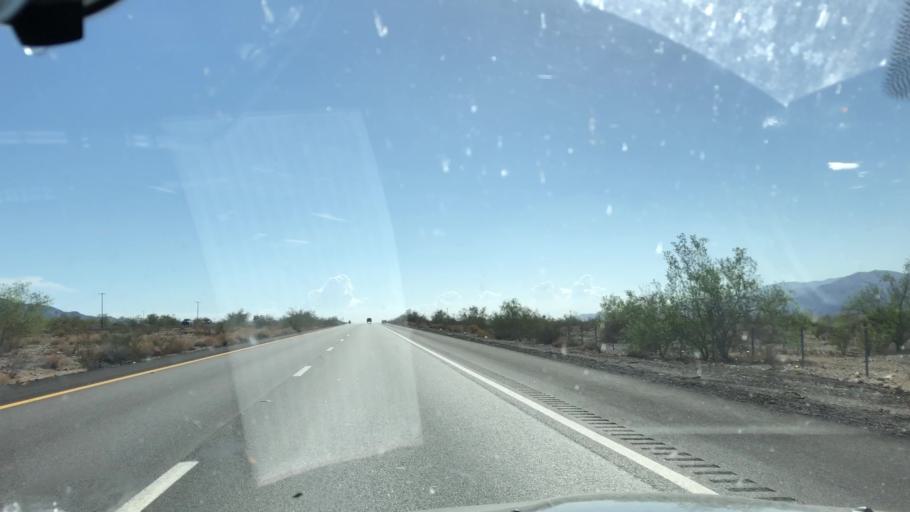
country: US
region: California
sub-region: Imperial County
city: Niland
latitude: 33.6895
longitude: -115.5115
